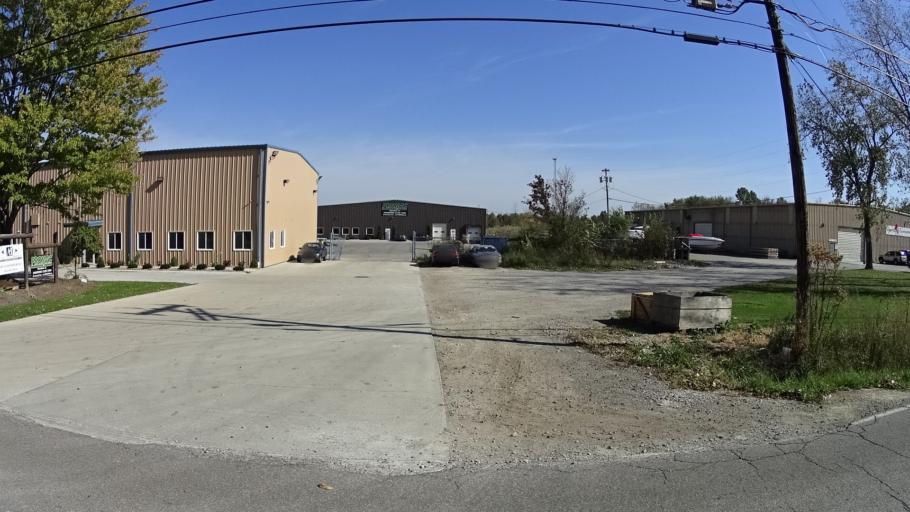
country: US
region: Ohio
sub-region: Lorain County
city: Vermilion-on-the-Lake
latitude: 41.4134
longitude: -82.3044
